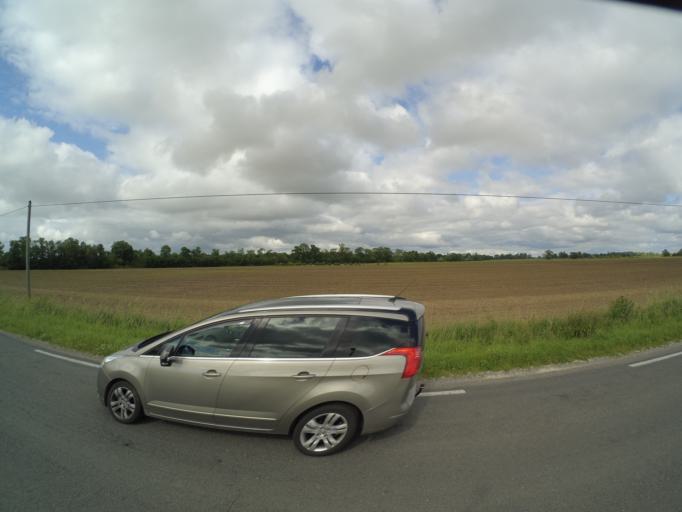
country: FR
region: Aquitaine
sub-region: Departement de la Gironde
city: Saint-Louis-de-Montferrand
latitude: 44.9788
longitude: -0.5623
